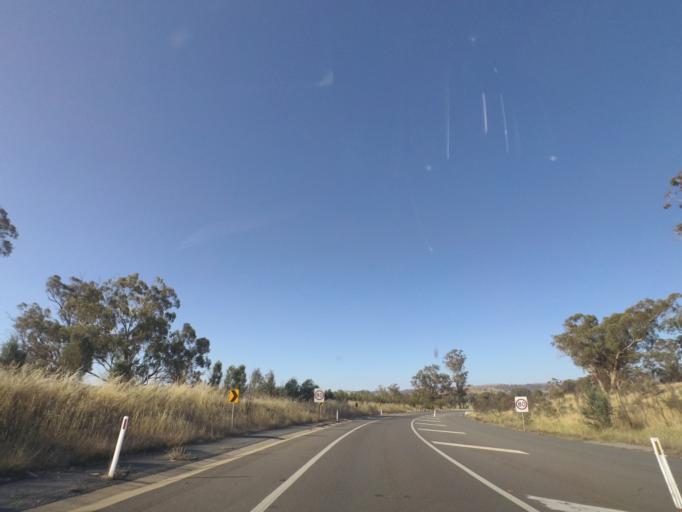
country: AU
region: New South Wales
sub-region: Wagga Wagga
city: Forest Hill
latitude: -35.2616
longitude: 147.7454
